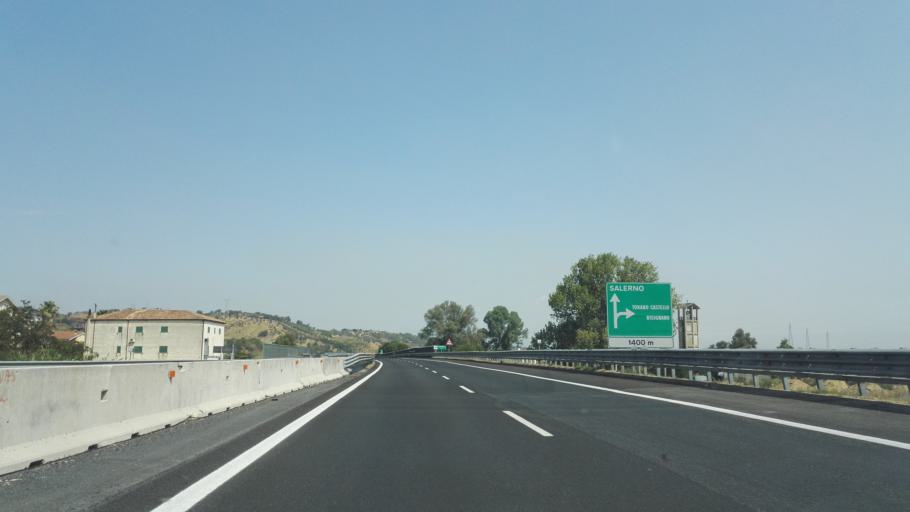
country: IT
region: Calabria
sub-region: Provincia di Cosenza
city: Sartano
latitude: 39.4944
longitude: 16.2117
